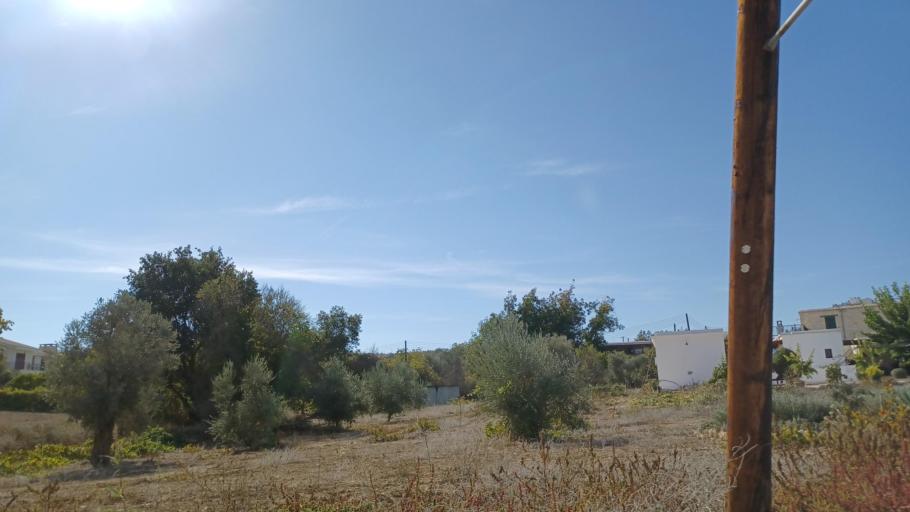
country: CY
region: Pafos
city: Pegeia
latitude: 34.9426
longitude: 32.4465
